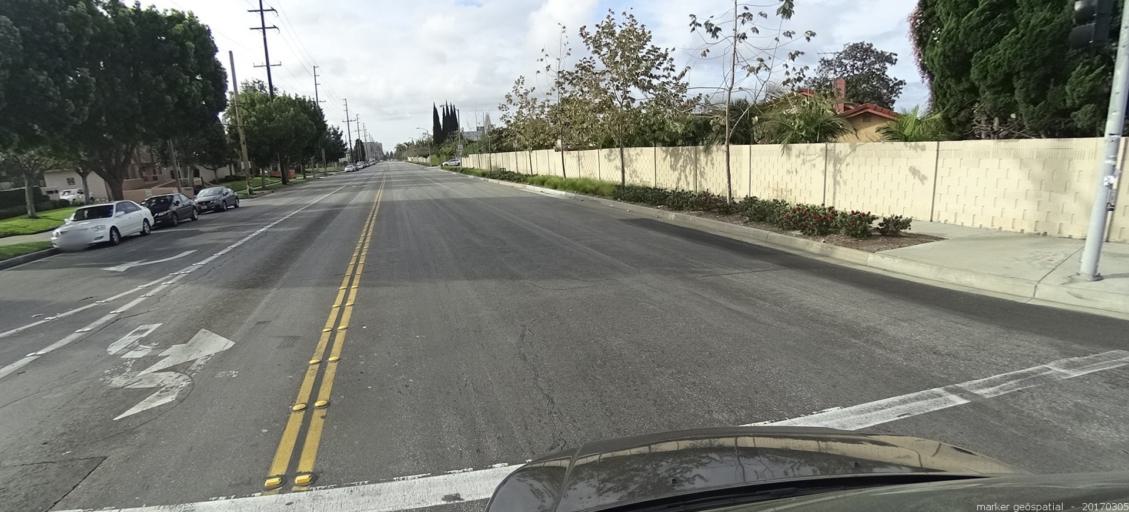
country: US
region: California
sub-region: Orange County
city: Anaheim
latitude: 33.7961
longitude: -117.8978
